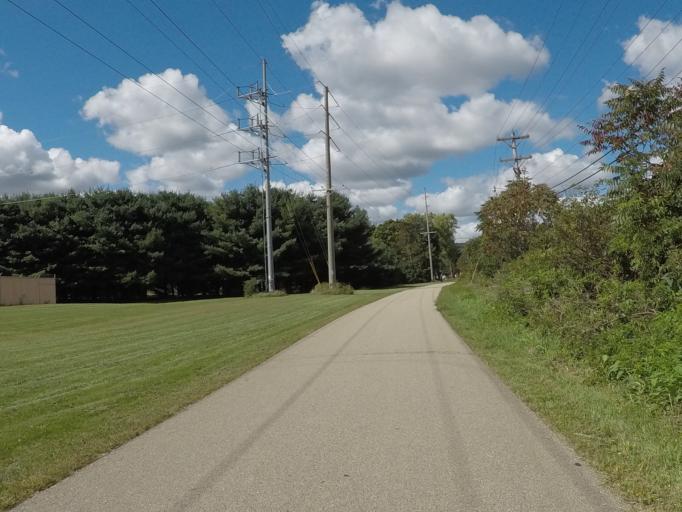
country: US
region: Wisconsin
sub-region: Richland County
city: Richland Center
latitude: 43.3202
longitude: -90.3769
